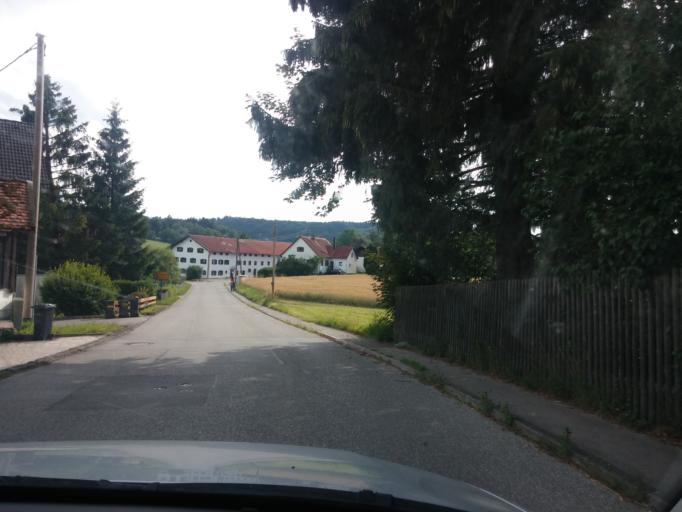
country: DE
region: Bavaria
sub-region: Upper Bavaria
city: Moosach
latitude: 48.0345
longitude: 11.8881
